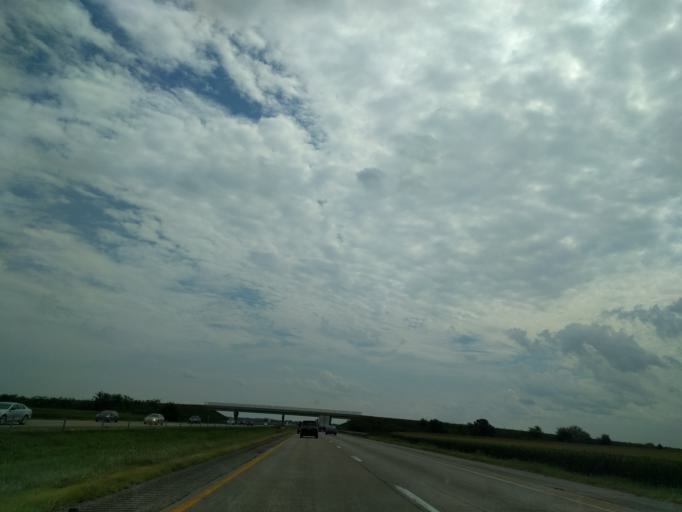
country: US
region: Indiana
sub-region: Newton County
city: Roselawn
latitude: 41.2486
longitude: -87.2956
